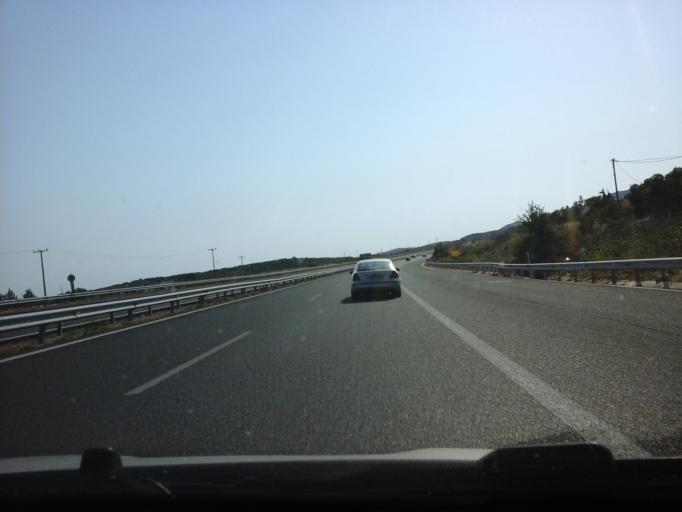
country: GR
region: East Macedonia and Thrace
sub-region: Nomos Evrou
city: Alexandroupoli
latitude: 40.8688
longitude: 25.7818
